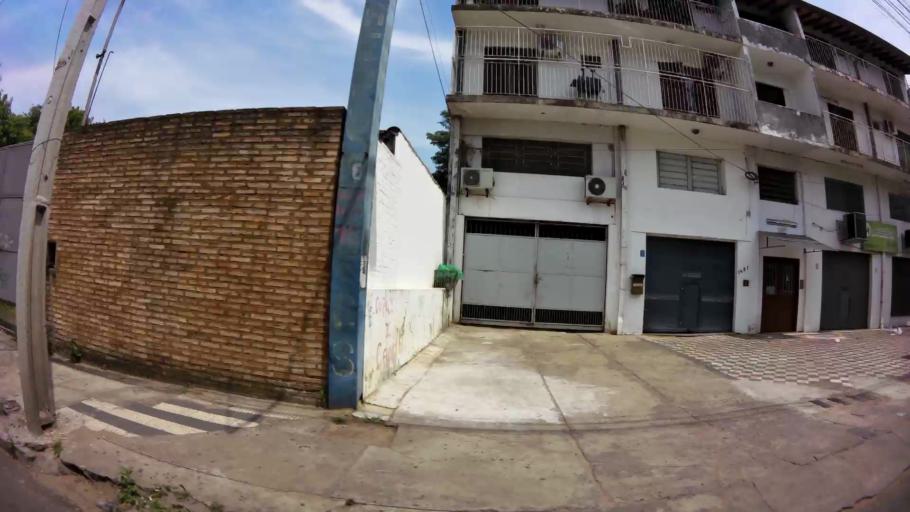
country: PY
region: Asuncion
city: Asuncion
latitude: -25.2745
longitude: -57.5852
